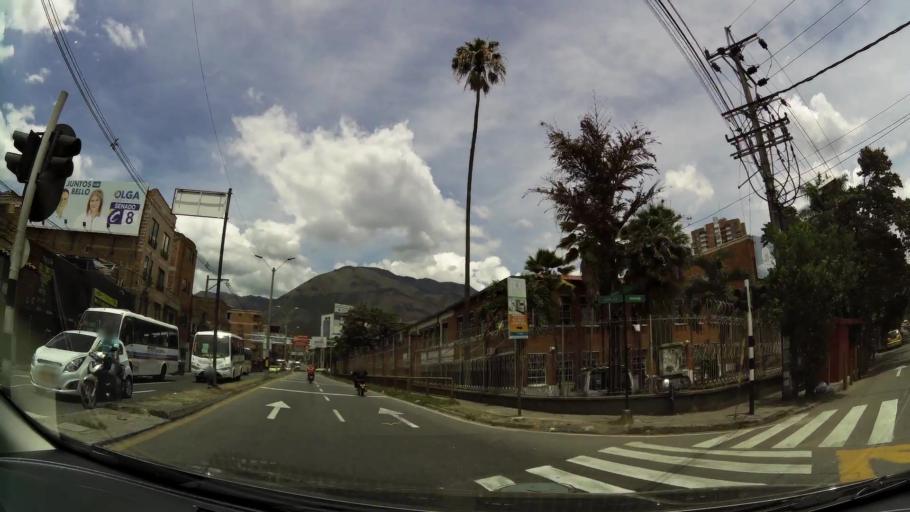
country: CO
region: Antioquia
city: Bello
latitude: 6.3300
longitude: -75.5580
